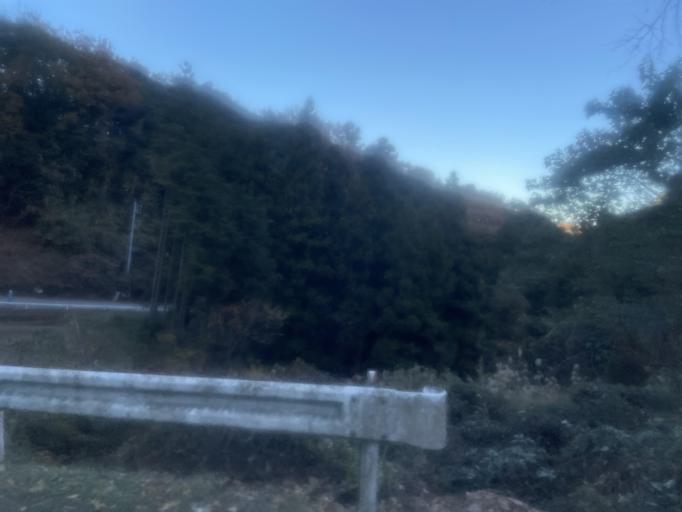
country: JP
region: Saitama
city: Yorii
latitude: 36.0908
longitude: 139.1728
